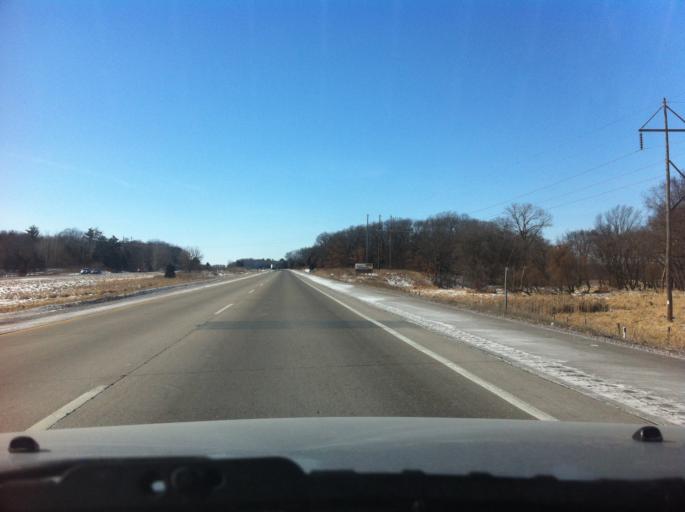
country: US
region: Wisconsin
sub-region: Columbia County
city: Portage
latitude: 43.5332
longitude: -89.5785
